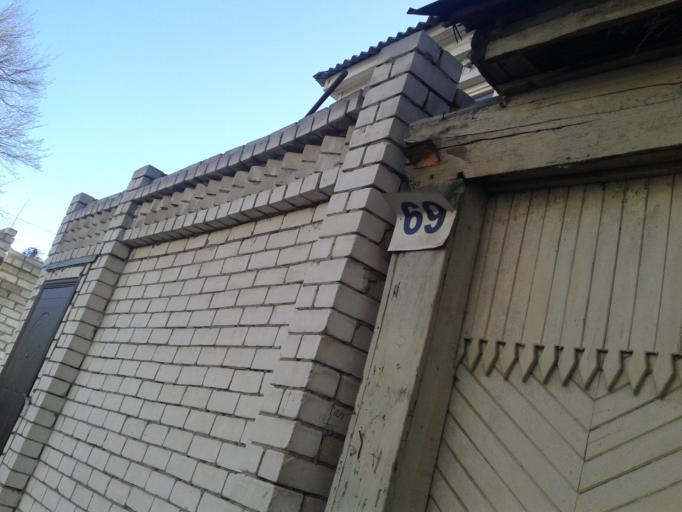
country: RU
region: Ulyanovsk
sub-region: Ulyanovskiy Rayon
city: Ulyanovsk
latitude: 54.2969
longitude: 48.3783
